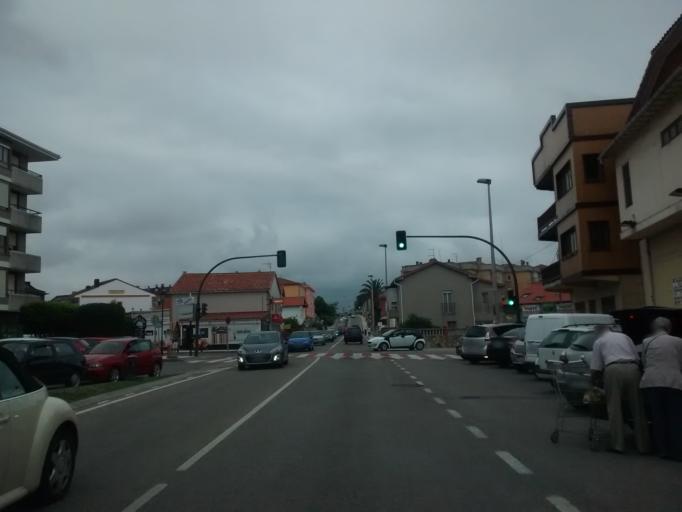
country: ES
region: Cantabria
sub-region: Provincia de Cantabria
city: Suances
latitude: 43.4252
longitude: -4.0405
